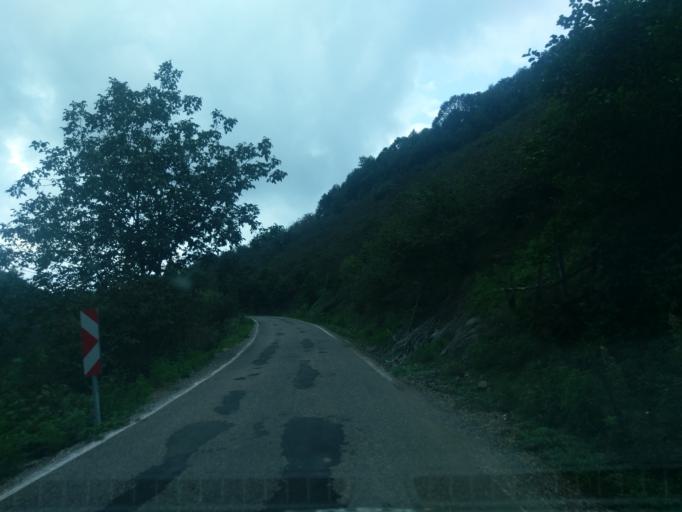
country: TR
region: Ordu
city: Gurgentepe
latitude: 40.8856
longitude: 37.6305
